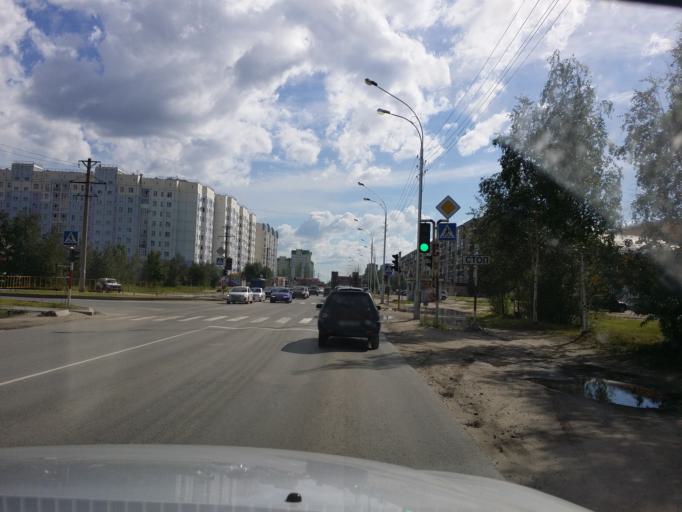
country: RU
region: Khanty-Mansiyskiy Avtonomnyy Okrug
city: Nizhnevartovsk
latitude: 60.9390
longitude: 76.6173
